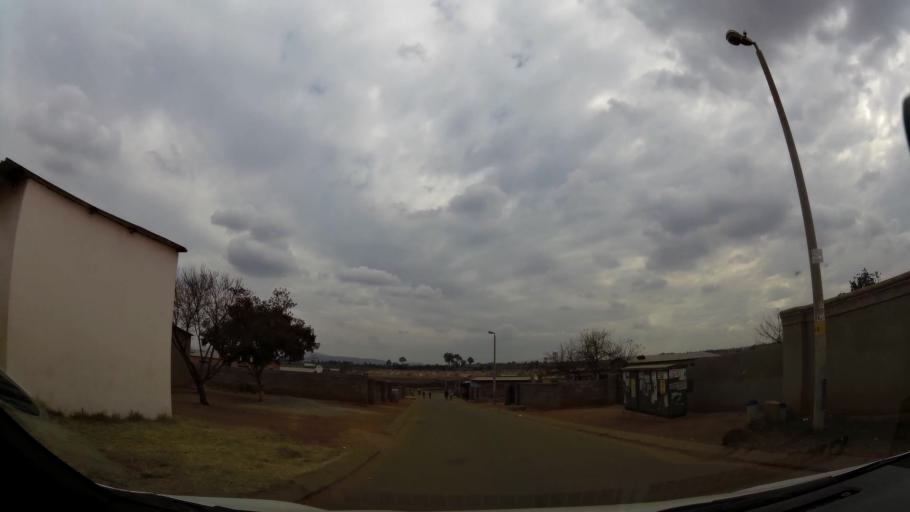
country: ZA
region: Gauteng
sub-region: Ekurhuleni Metropolitan Municipality
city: Germiston
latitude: -26.3751
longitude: 28.1190
